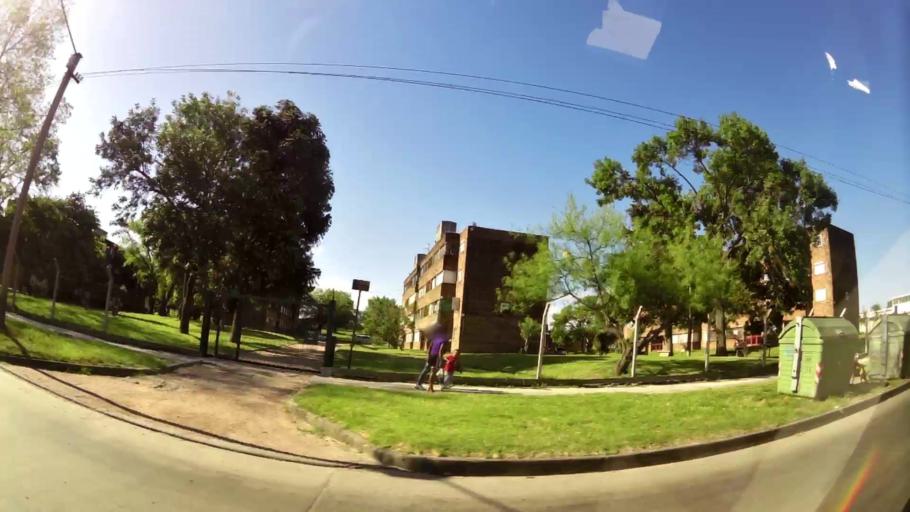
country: UY
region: Montevideo
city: Montevideo
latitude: -34.8335
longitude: -56.1487
